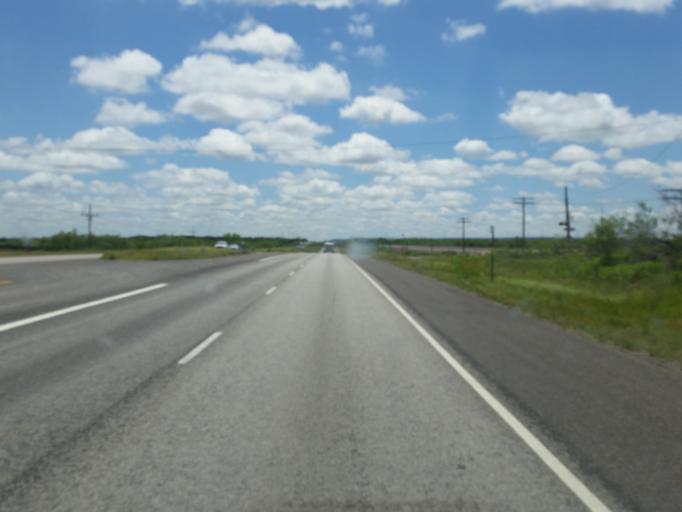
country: US
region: Texas
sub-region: Garza County
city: Post
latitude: 33.0368
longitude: -101.1968
